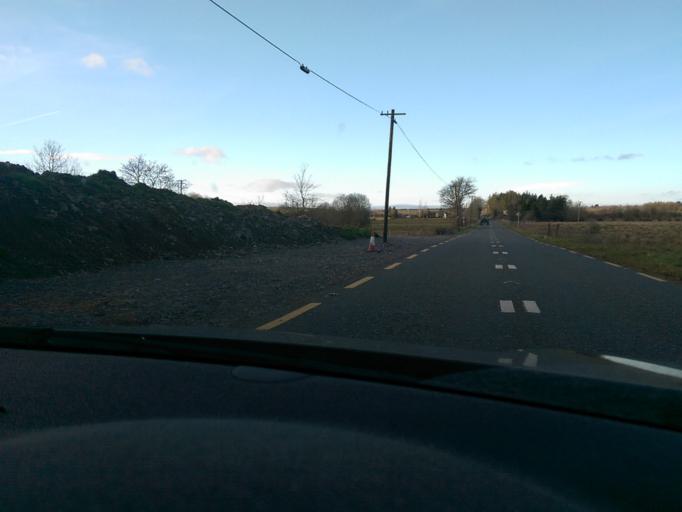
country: IE
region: Connaught
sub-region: Roscommon
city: Boyle
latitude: 53.9255
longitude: -8.2777
